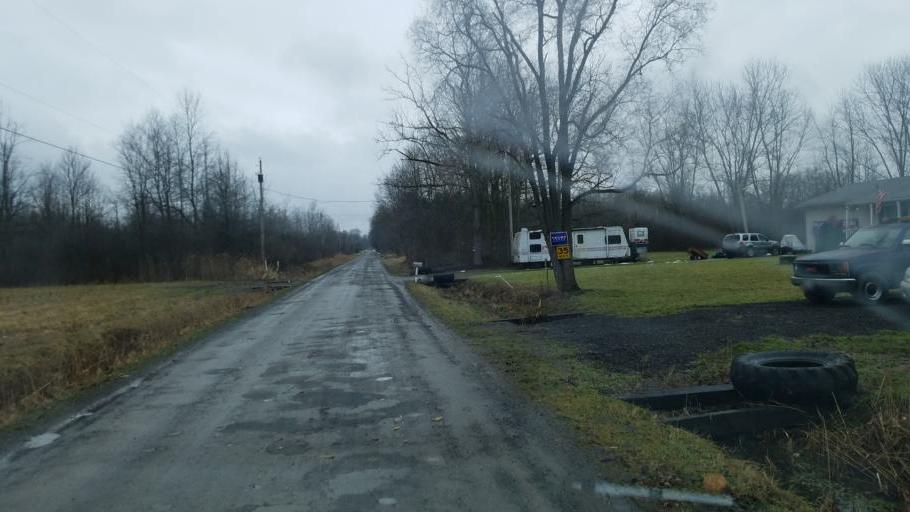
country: US
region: Ohio
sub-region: Ashtabula County
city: Orwell
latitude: 41.4546
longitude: -80.9347
